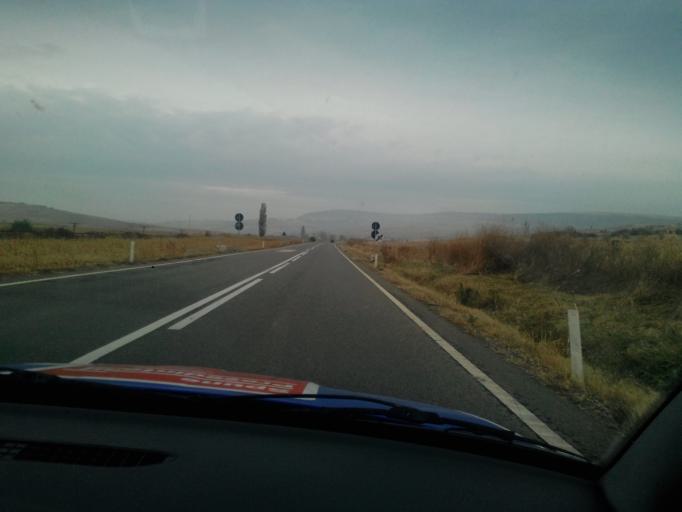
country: RO
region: Vaslui
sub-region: Comuna Albesti
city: Corni-Albesti
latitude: 46.5415
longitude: 27.8422
